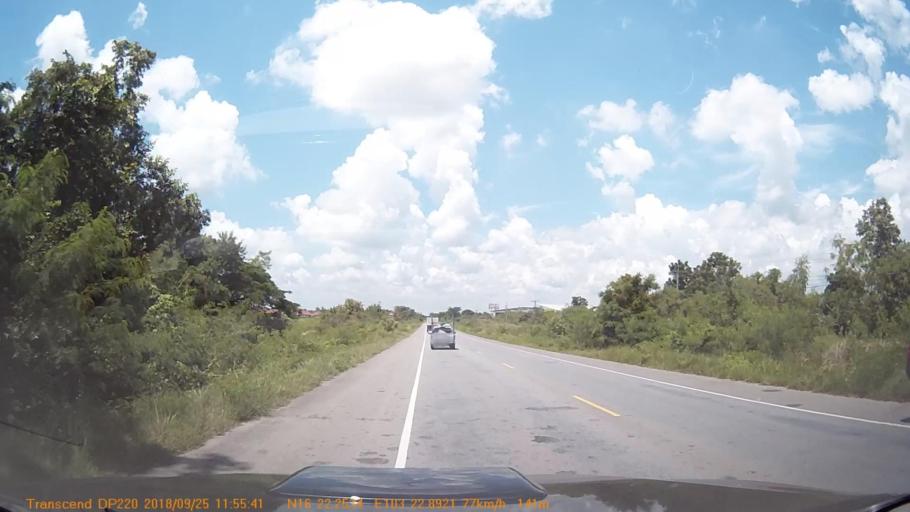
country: TH
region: Kalasin
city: Yang Talat
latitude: 16.3709
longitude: 103.3815
